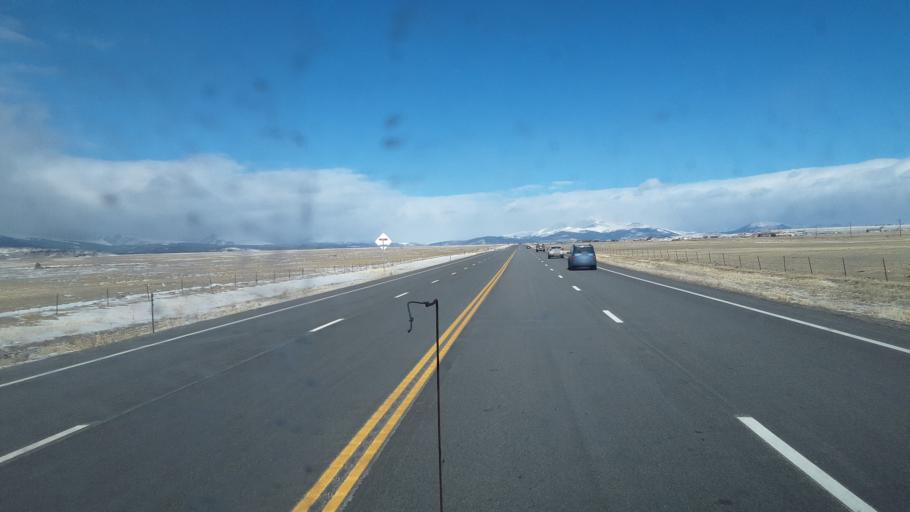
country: US
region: Colorado
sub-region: Park County
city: Fairplay
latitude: 39.1113
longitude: -105.9916
